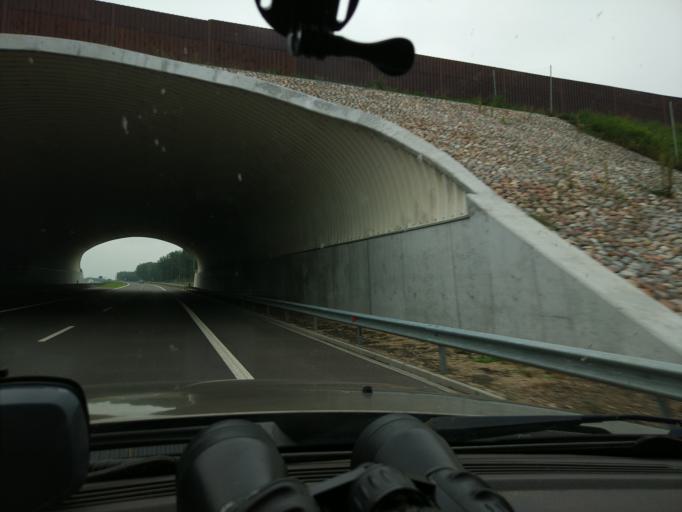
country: PL
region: Podlasie
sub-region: Powiat zambrowski
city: Szumowo
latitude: 52.9307
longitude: 22.1356
